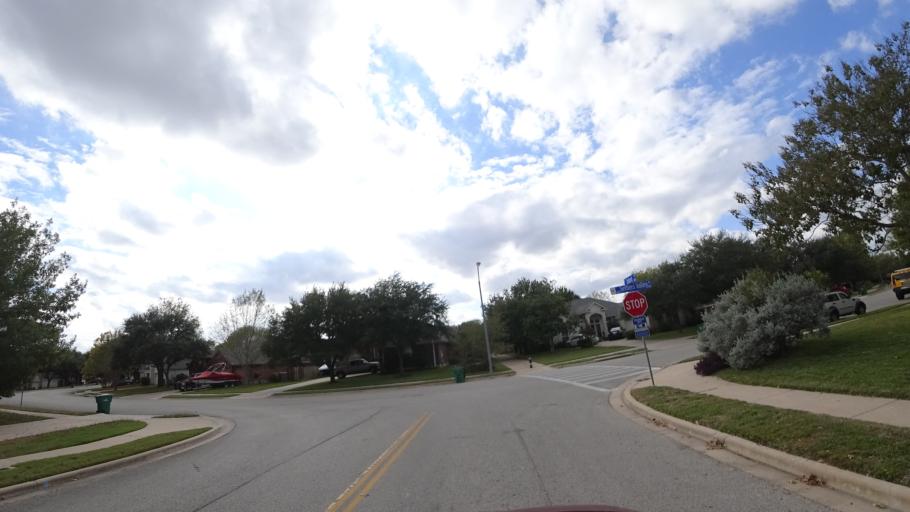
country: US
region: Texas
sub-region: Travis County
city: Pflugerville
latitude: 30.4344
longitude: -97.6269
